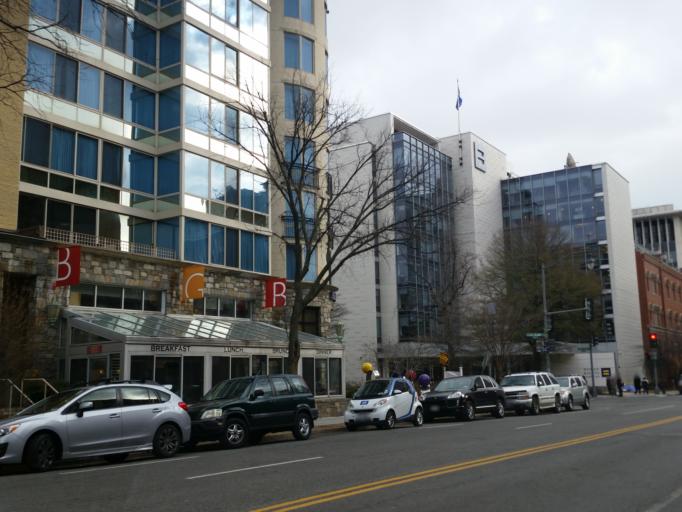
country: US
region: Washington, D.C.
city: Washington, D.C.
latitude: 38.9072
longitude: -77.0386
